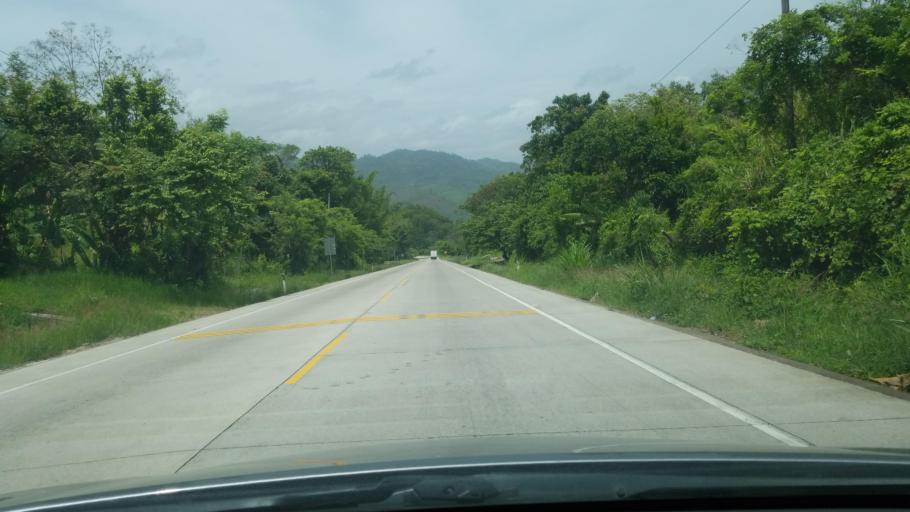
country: HN
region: Copan
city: Quezailica
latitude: 14.9072
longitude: -88.7530
